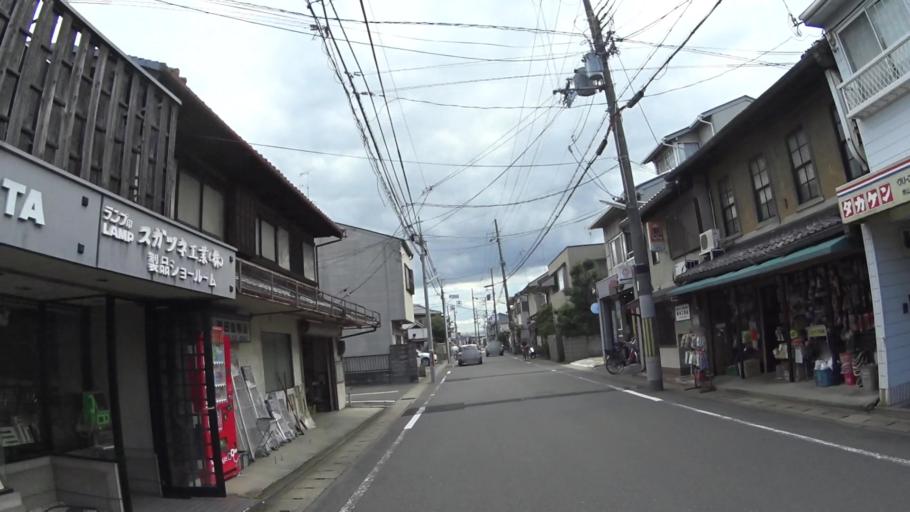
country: JP
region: Kyoto
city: Yawata
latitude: 34.8989
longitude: 135.7172
